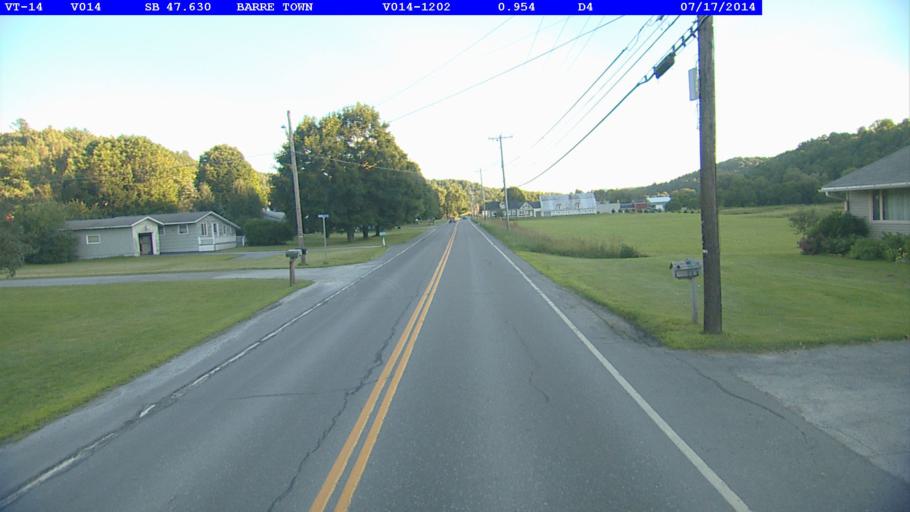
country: US
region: Vermont
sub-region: Washington County
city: South Barre
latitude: 44.1632
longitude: -72.5119
